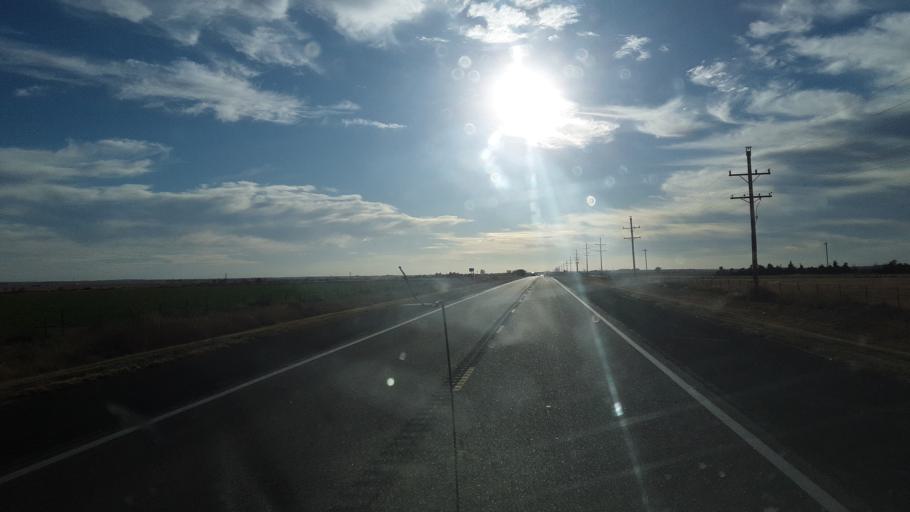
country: US
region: Kansas
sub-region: Kearny County
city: Lakin
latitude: 37.9692
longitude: -101.2006
